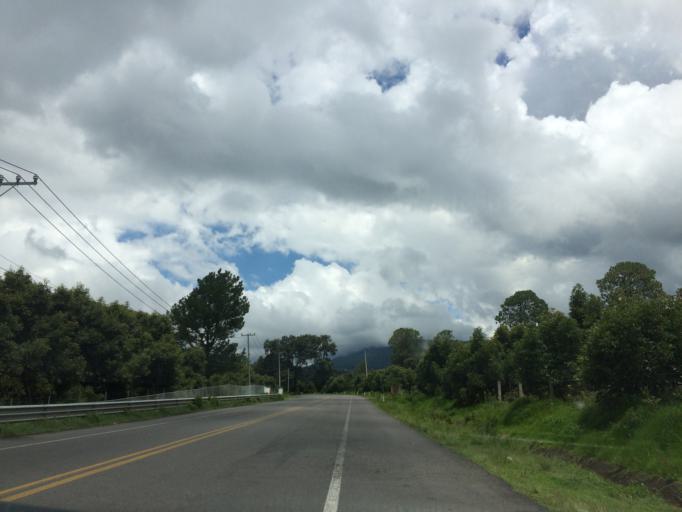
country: MX
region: Michoacan
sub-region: Uruapan
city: Santa Ana Zirosto
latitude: 19.5526
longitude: -102.3060
